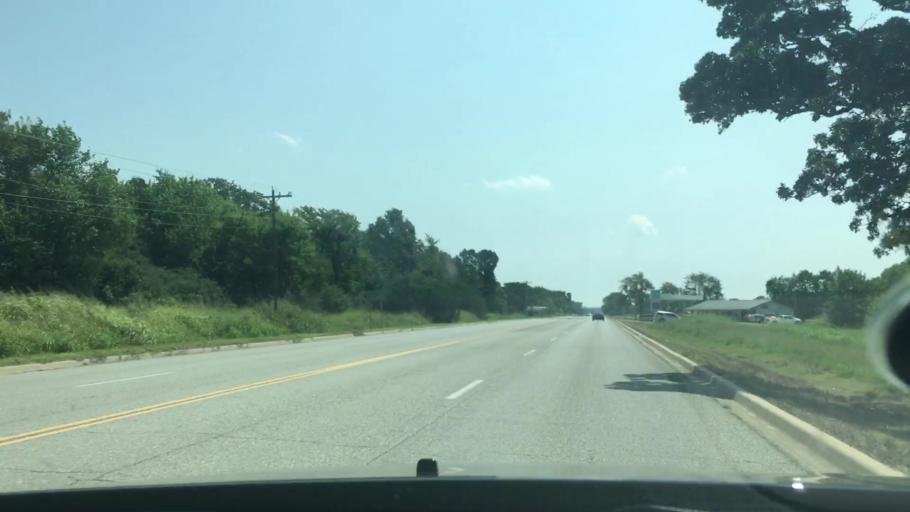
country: US
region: Oklahoma
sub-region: Atoka County
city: Atoka
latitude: 34.3031
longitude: -95.9990
